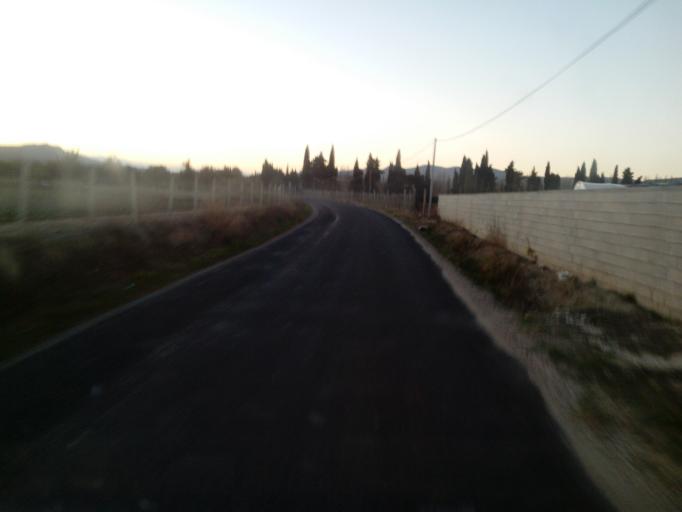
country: FR
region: Languedoc-Roussillon
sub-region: Departement des Pyrenees-Orientales
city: Rivesaltes
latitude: 42.7700
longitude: 2.8618
